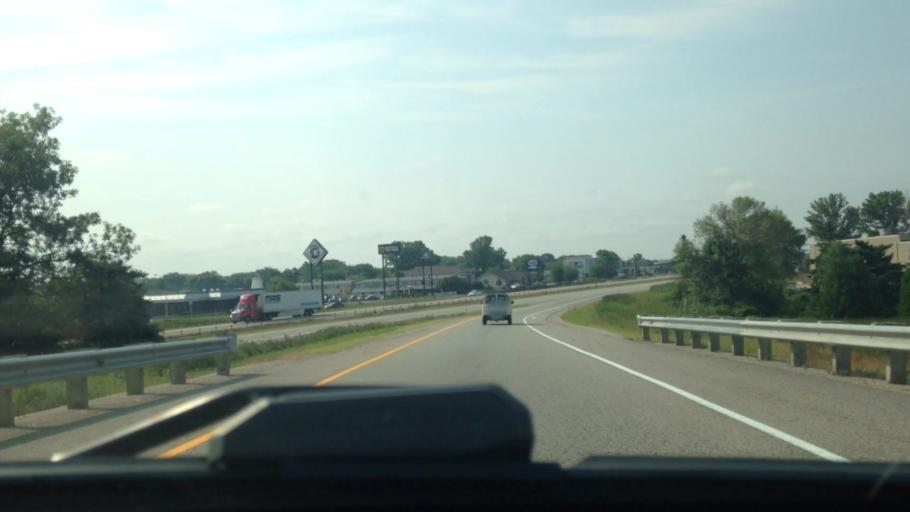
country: US
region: Wisconsin
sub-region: Fond du Lac County
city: North Fond du Lac
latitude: 43.7841
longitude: -88.4835
